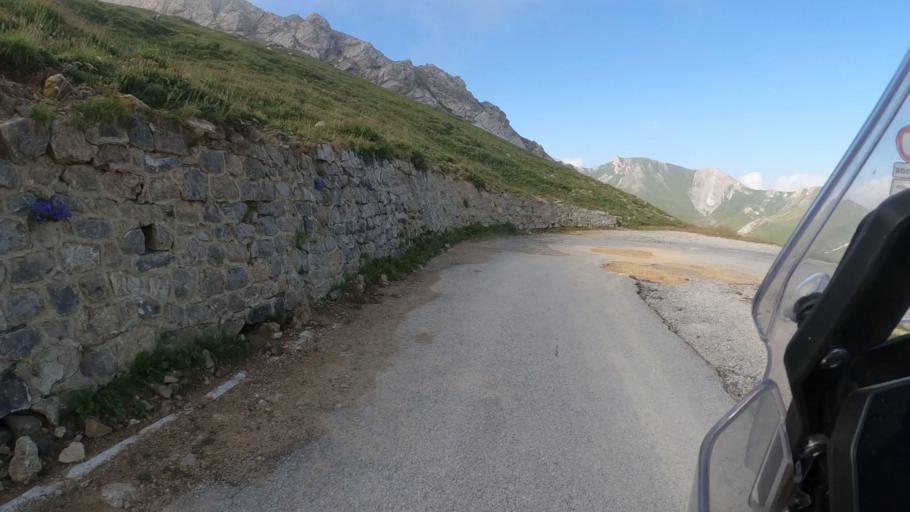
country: IT
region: Piedmont
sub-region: Provincia di Cuneo
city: Sambuco
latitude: 44.3808
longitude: 7.1005
